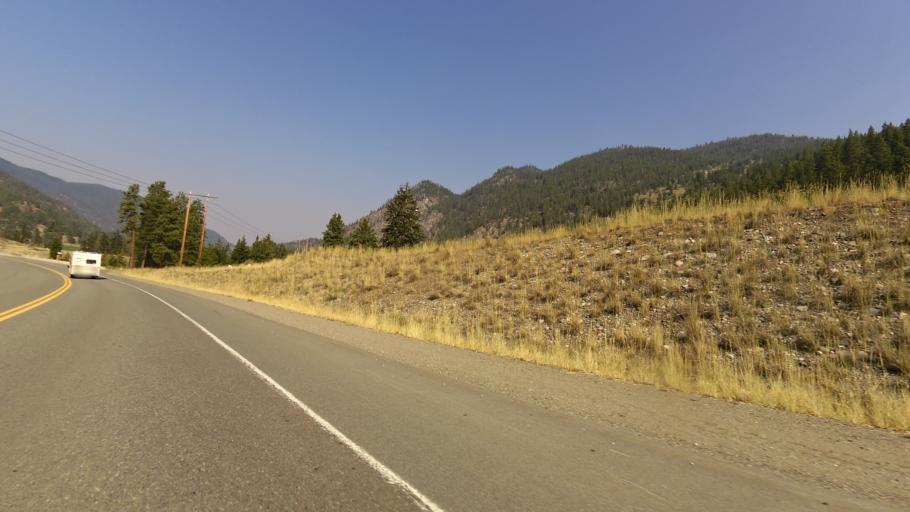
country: CA
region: British Columbia
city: Princeton
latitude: 49.3778
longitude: -120.1506
